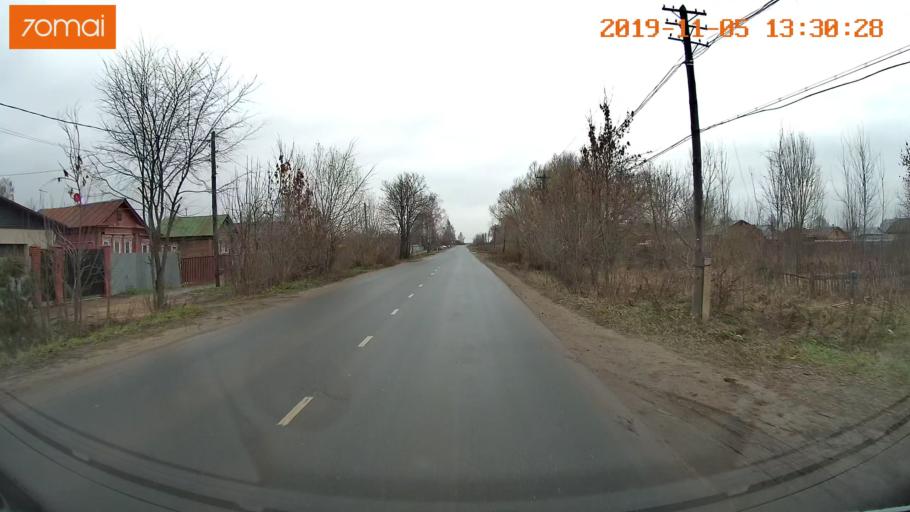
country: RU
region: Ivanovo
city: Shuya
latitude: 56.8672
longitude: 41.3960
